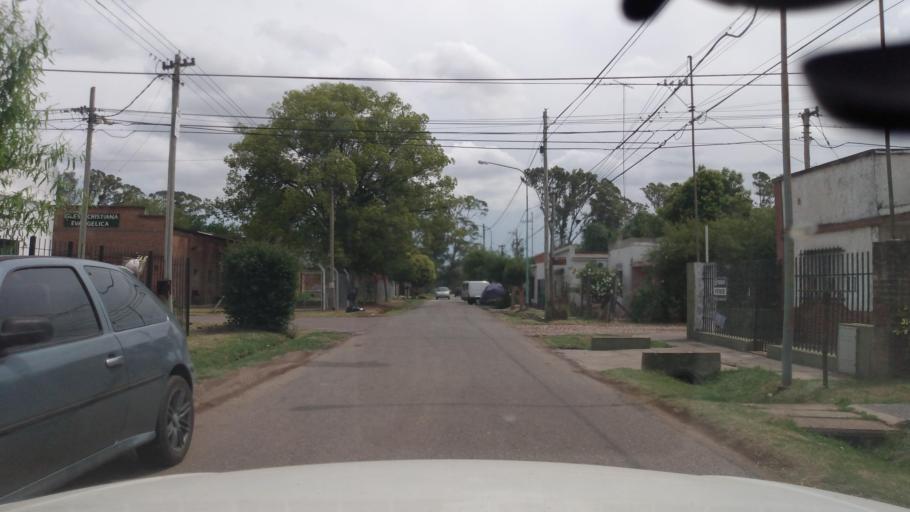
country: AR
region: Buenos Aires
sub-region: Partido de Lujan
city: Lujan
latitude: -34.5572
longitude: -59.2066
